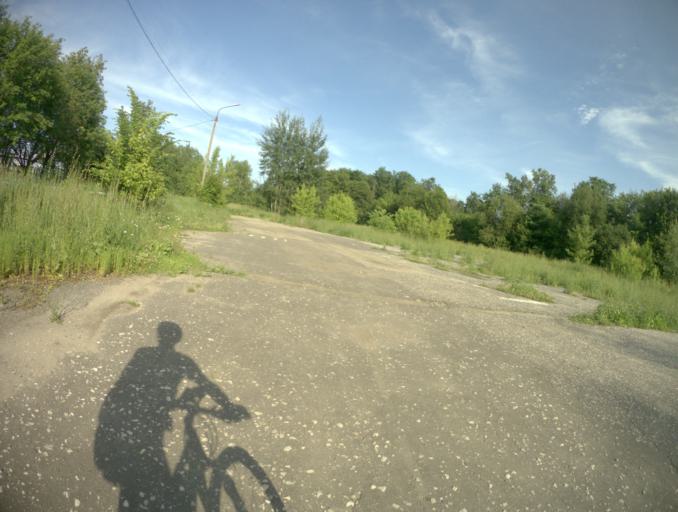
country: RU
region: Vladimir
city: Suzdal'
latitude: 56.4281
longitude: 40.4487
